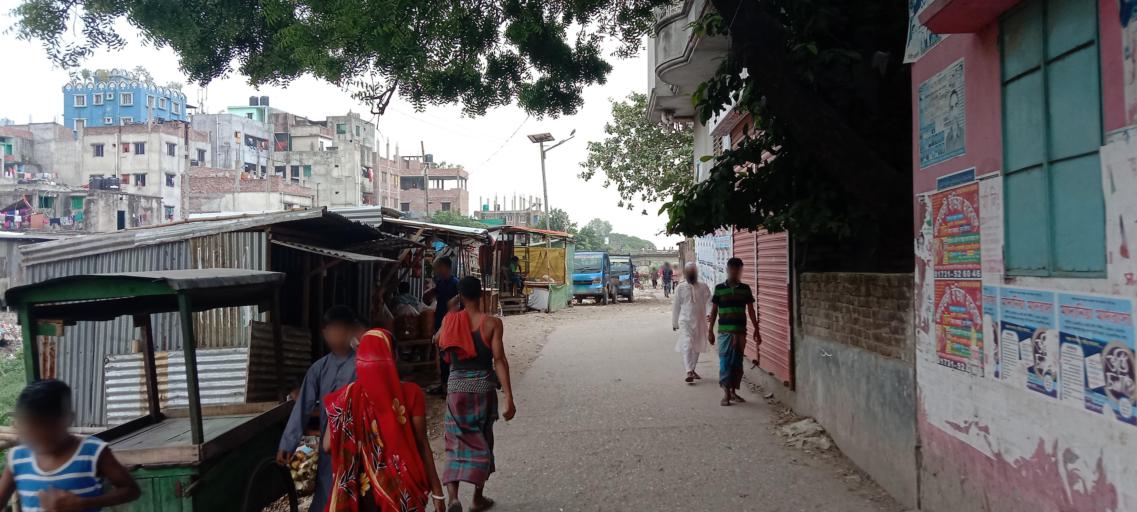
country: BD
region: Dhaka
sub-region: Dhaka
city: Dhaka
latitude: 23.6988
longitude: 90.4091
